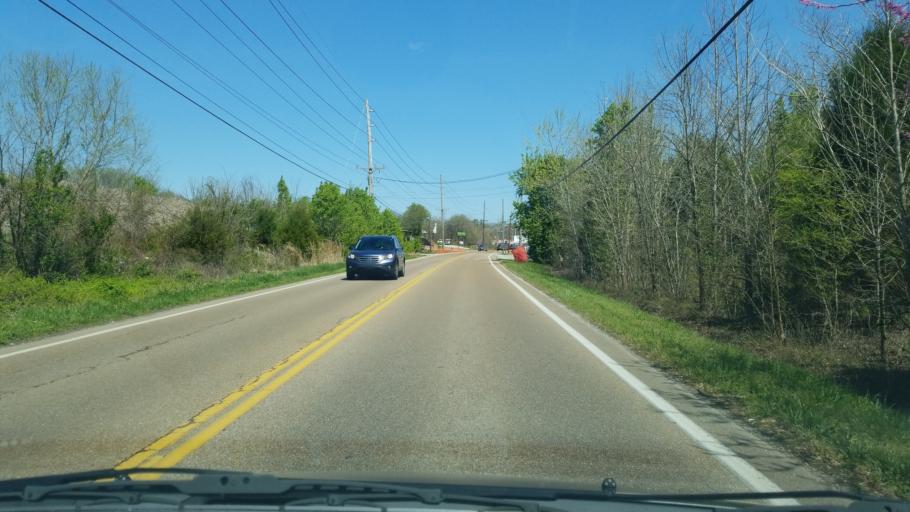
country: US
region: Tennessee
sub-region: Hamilton County
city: Middle Valley
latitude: 35.1669
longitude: -85.2098
